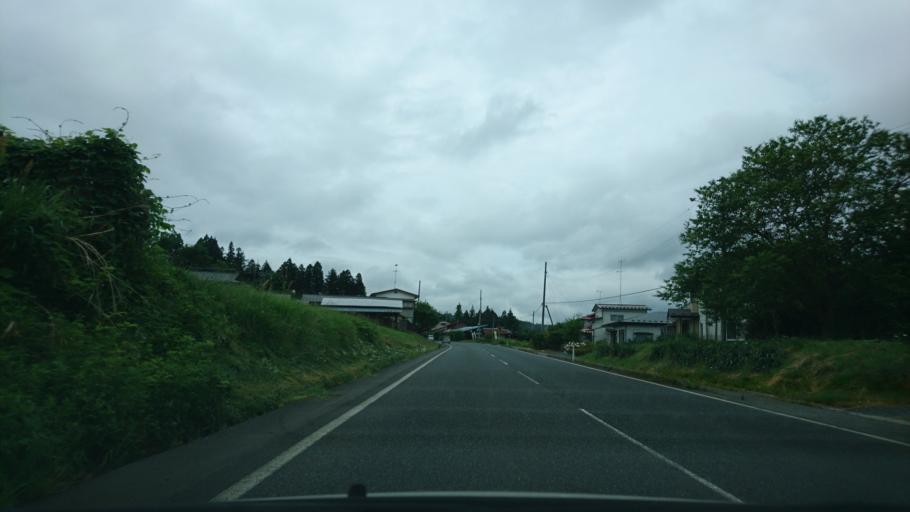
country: JP
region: Iwate
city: Ichinoseki
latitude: 38.8931
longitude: 141.1227
